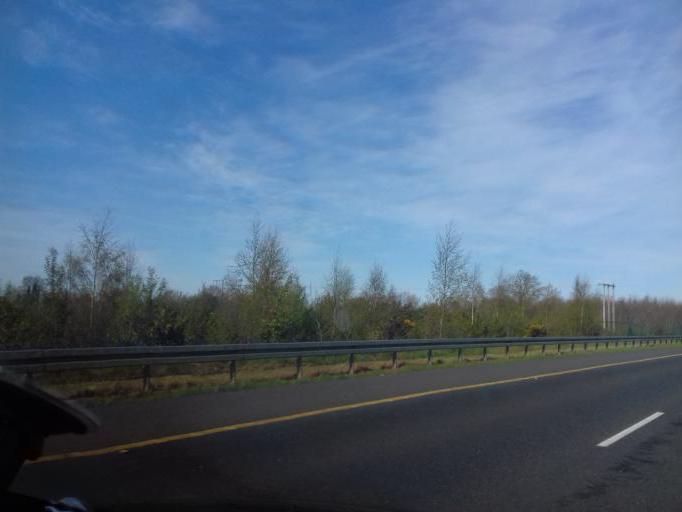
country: IE
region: Leinster
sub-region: An Mhi
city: Navan
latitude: 53.6196
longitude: -6.7046
